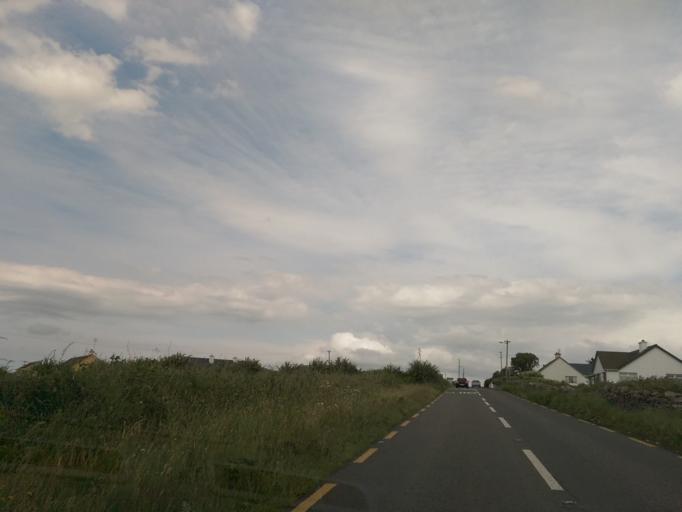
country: IE
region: Munster
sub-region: An Clar
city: Kilrush
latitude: 52.8458
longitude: -9.4194
